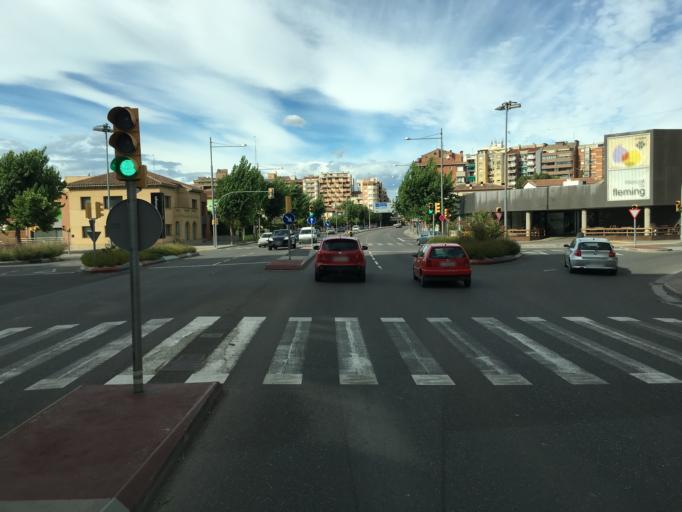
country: ES
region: Catalonia
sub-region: Provincia de Lleida
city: Lleida
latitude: 41.6195
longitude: 0.6152
